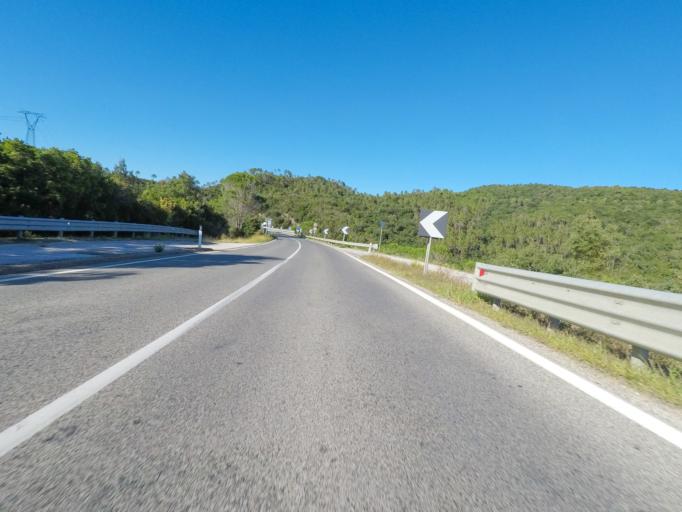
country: IT
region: Tuscany
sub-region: Provincia di Grosseto
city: Civitella Marittima
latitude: 43.0131
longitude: 11.2882
